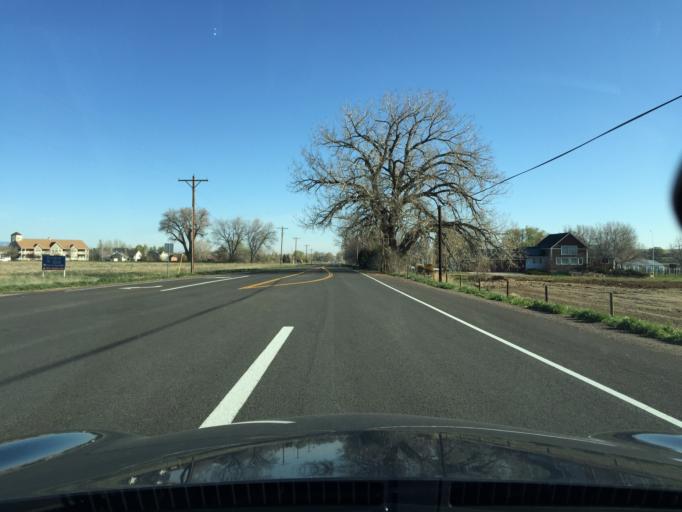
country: US
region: Colorado
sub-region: Boulder County
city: Erie
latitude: 40.0587
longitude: -105.0554
